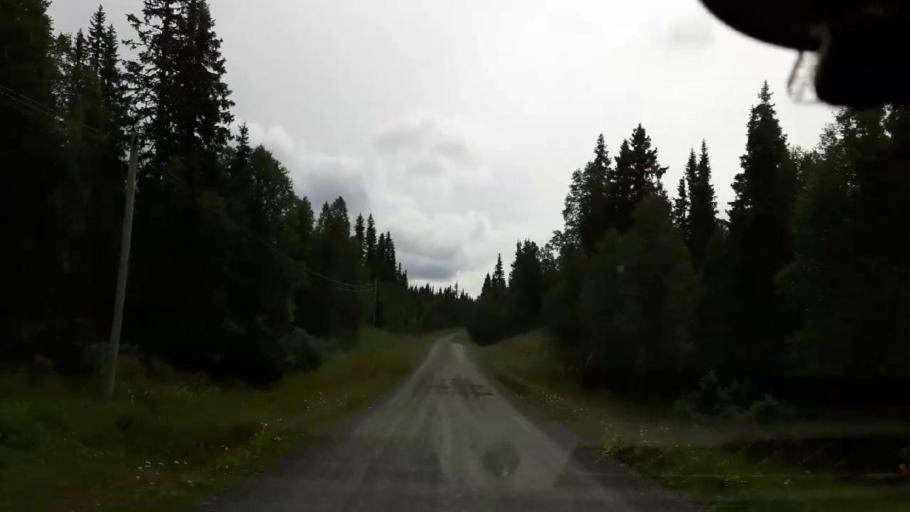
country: SE
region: Jaemtland
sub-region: Krokoms Kommun
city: Valla
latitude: 63.7668
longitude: 13.8342
